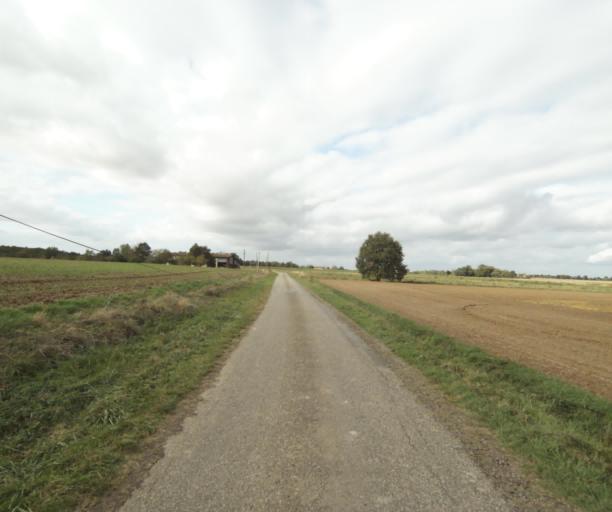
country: FR
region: Midi-Pyrenees
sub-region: Departement du Tarn-et-Garonne
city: Beaumont-de-Lomagne
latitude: 43.8829
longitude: 1.0852
